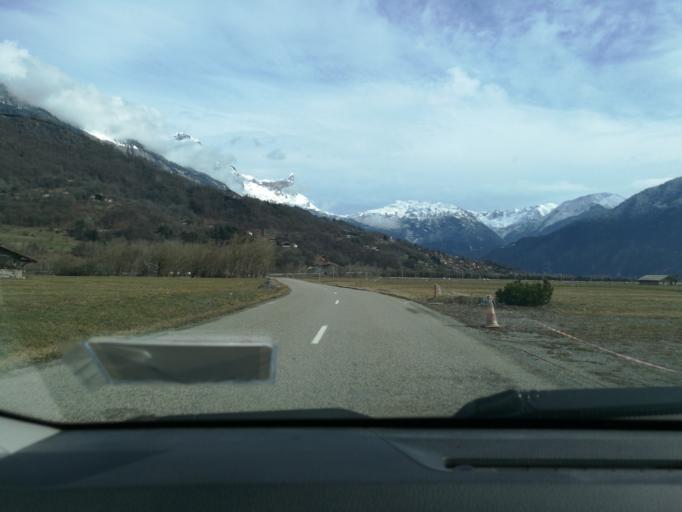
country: FR
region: Rhone-Alpes
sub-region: Departement de la Haute-Savoie
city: Domancy
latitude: 45.9159
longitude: 6.6631
